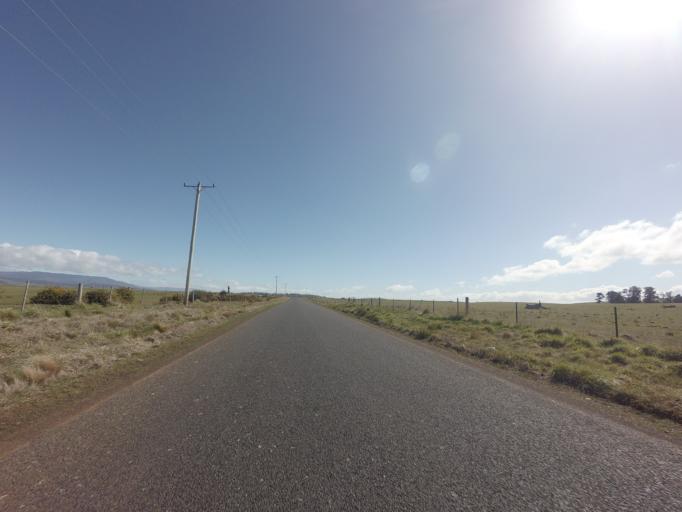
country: AU
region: Tasmania
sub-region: Northern Midlands
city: Evandale
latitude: -41.9022
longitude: 147.4471
